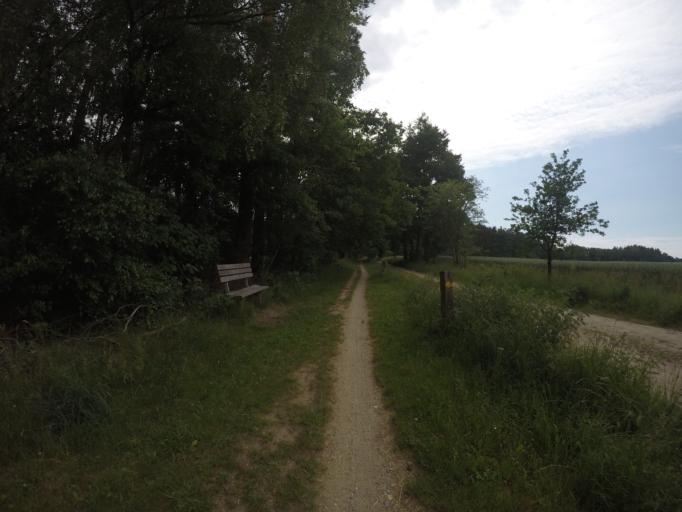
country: DE
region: Lower Saxony
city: Undeloh
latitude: 53.2017
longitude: 9.9760
